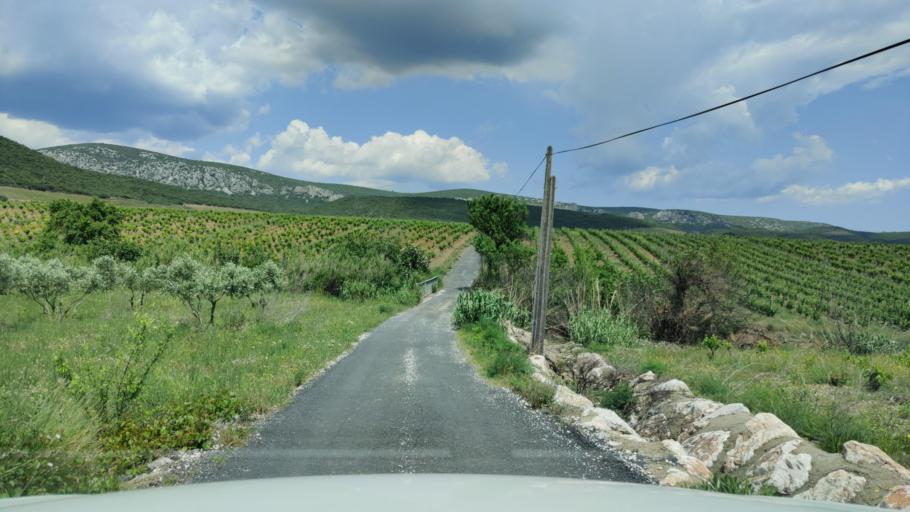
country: FR
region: Languedoc-Roussillon
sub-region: Departement des Pyrenees-Orientales
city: Estagel
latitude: 42.8124
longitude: 2.6696
